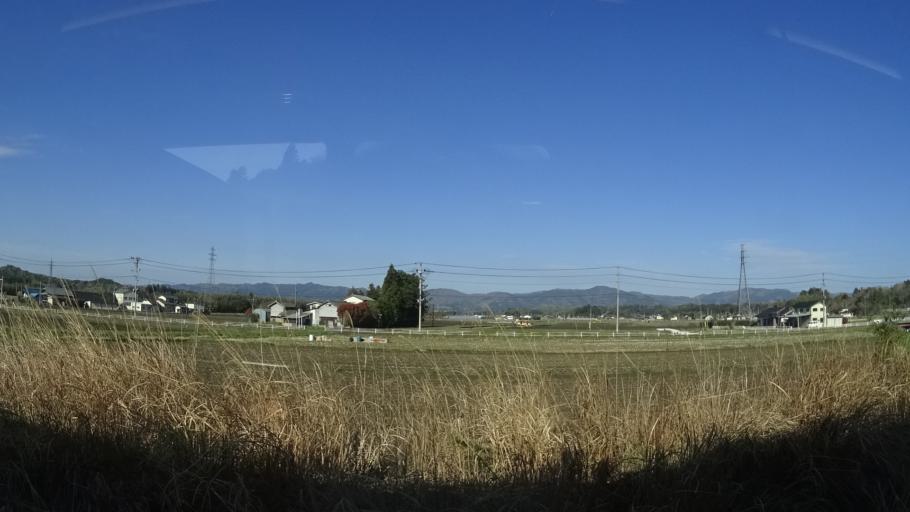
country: JP
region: Fukushima
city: Namie
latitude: 37.6108
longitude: 140.9857
